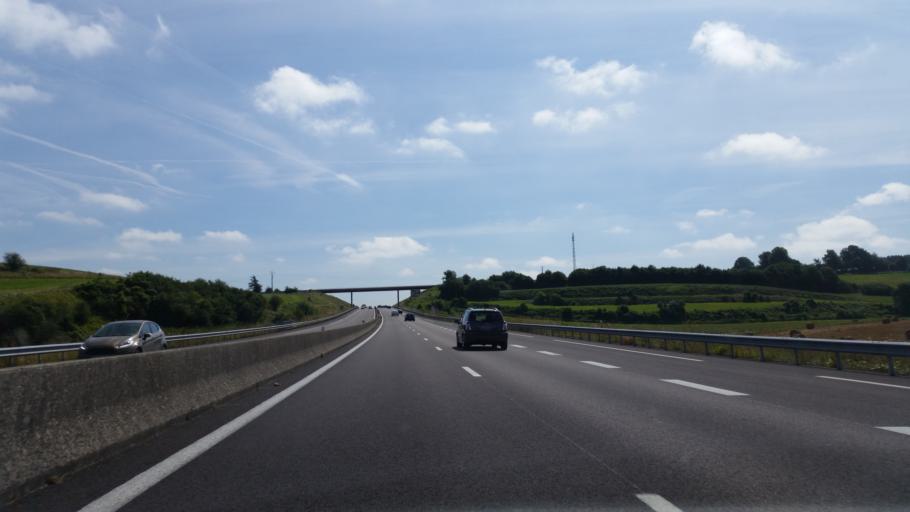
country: FR
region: Haute-Normandie
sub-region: Departement de la Seine-Maritime
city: Neufchatel-en-Bray
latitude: 49.7409
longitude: 1.5375
